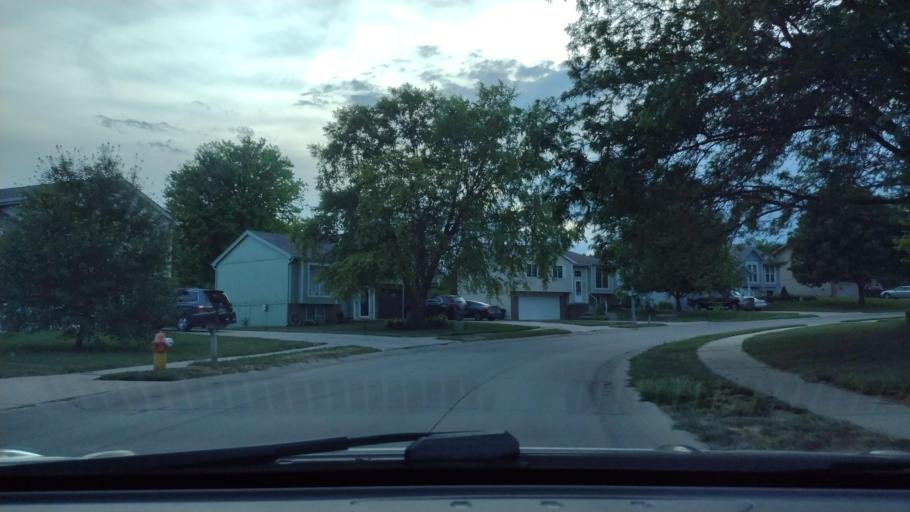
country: US
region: Nebraska
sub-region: Sarpy County
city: Offutt Air Force Base
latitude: 41.1514
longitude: -95.9421
